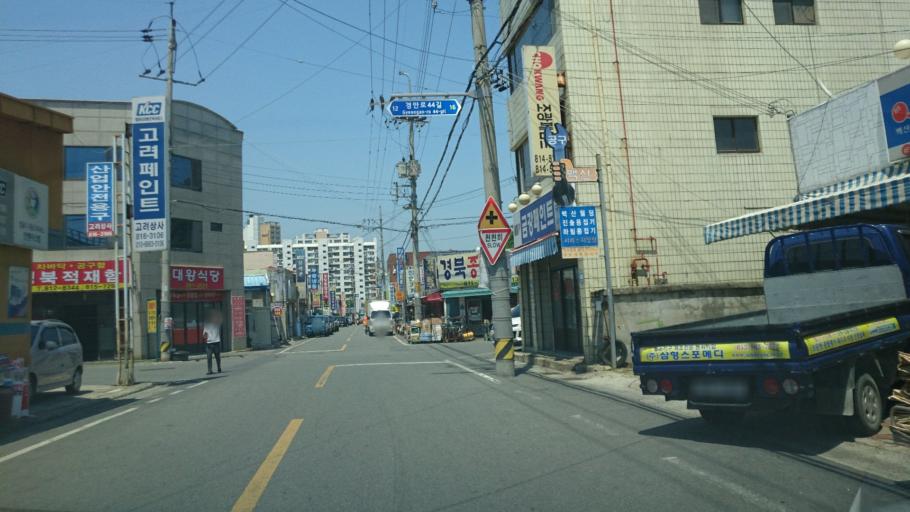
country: KR
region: Gyeongsangbuk-do
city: Gyeongsan-si
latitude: 35.8269
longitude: 128.7381
